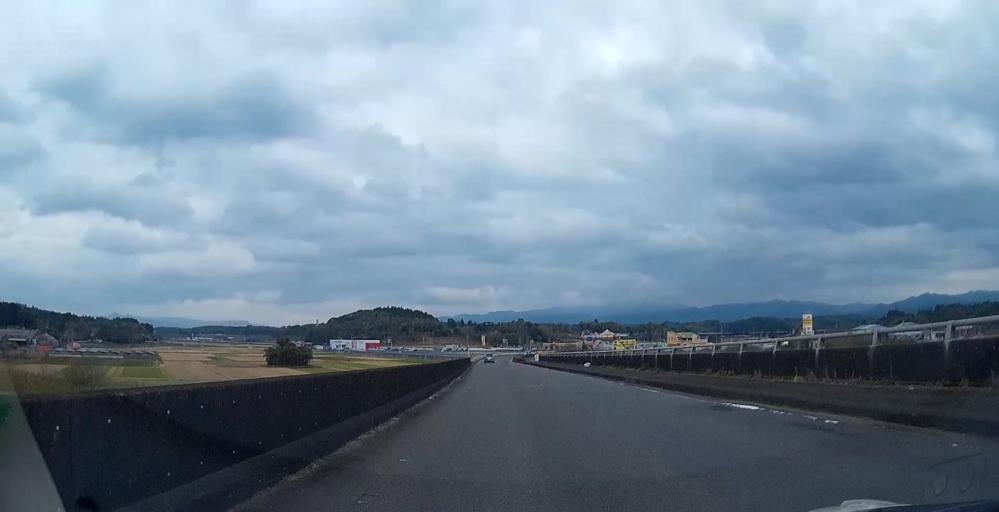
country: JP
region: Kagoshima
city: Akune
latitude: 32.0636
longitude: 130.2236
